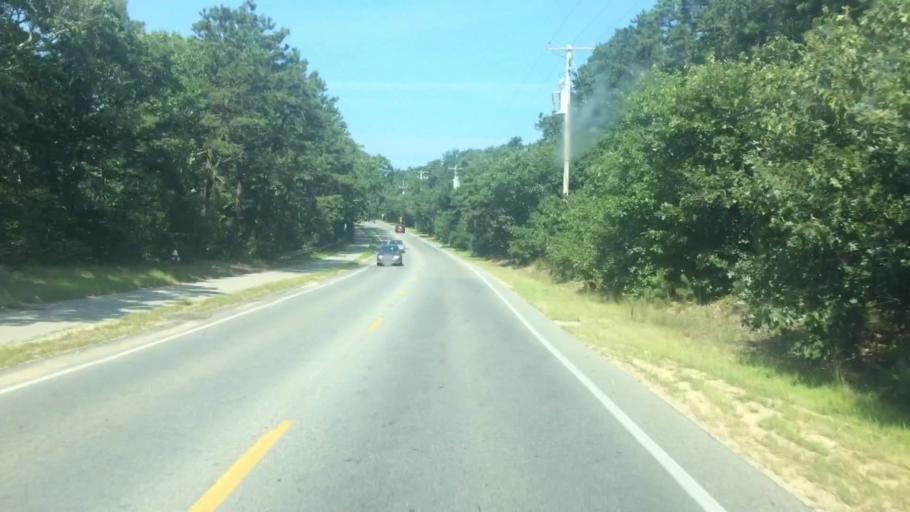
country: US
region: Massachusetts
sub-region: Dukes County
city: Oak Bluffs
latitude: 41.4139
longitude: -70.5785
